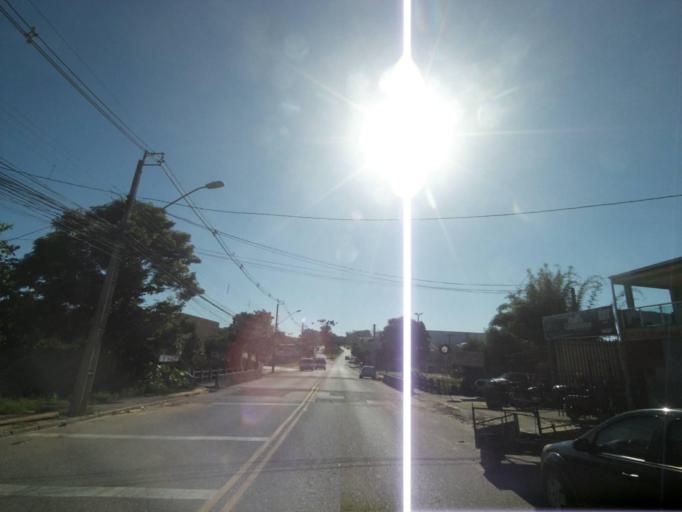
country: BR
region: Parana
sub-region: Curitiba
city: Curitiba
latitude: -25.4647
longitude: -49.3518
